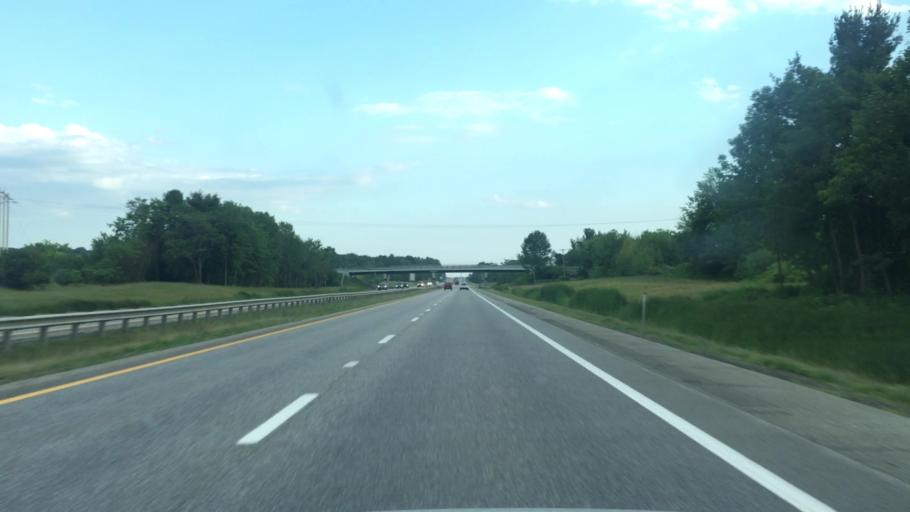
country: US
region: Maine
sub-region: Kennebec County
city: Hallowell
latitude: 44.2998
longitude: -69.8076
